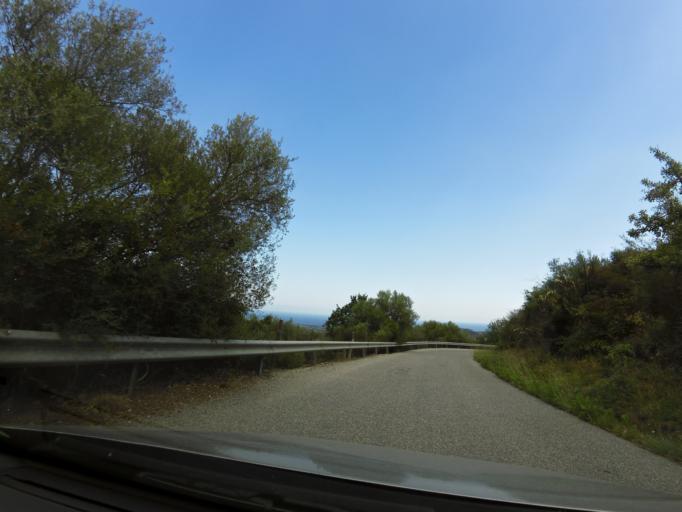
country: IT
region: Calabria
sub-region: Provincia di Reggio Calabria
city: Camini
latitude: 38.4351
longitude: 16.5146
